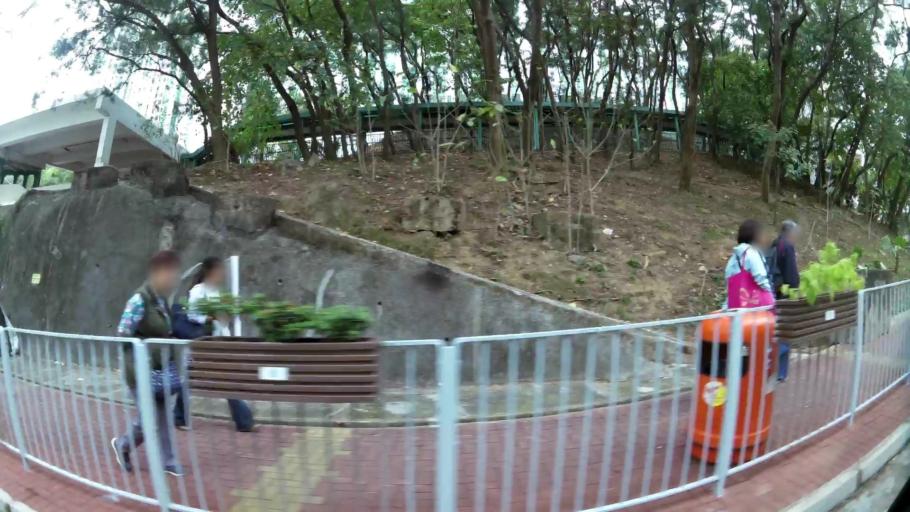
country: HK
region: Tsuen Wan
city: Tsuen Wan
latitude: 22.3777
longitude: 114.1042
